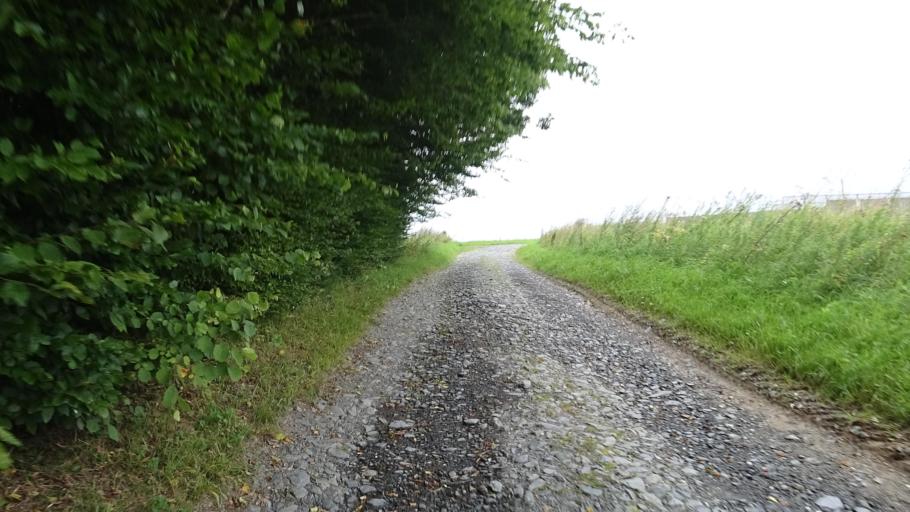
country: BE
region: Wallonia
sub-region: Province du Luxembourg
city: Chiny
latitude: 49.8057
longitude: 5.3269
